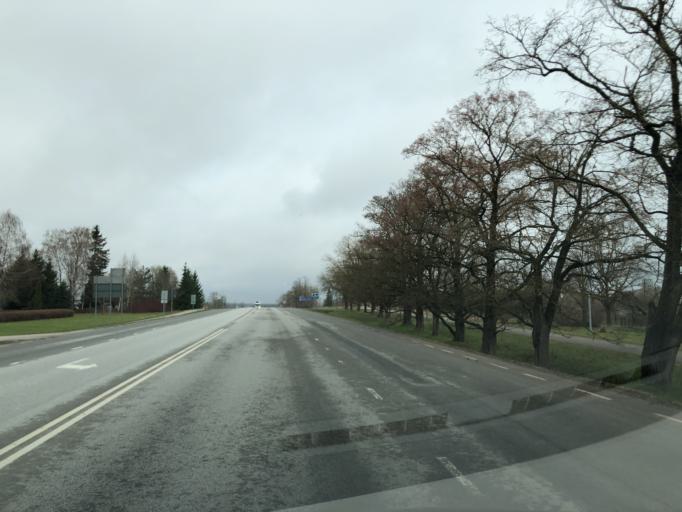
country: EE
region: Jogevamaa
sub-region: Jogeva linn
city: Jogeva
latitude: 58.7427
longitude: 26.3663
